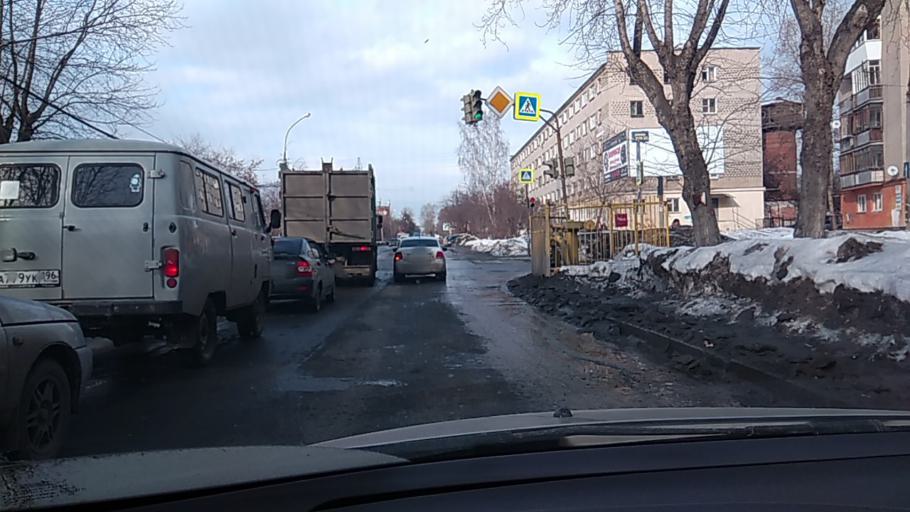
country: RU
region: Sverdlovsk
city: Yekaterinburg
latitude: 56.8649
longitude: 60.6530
